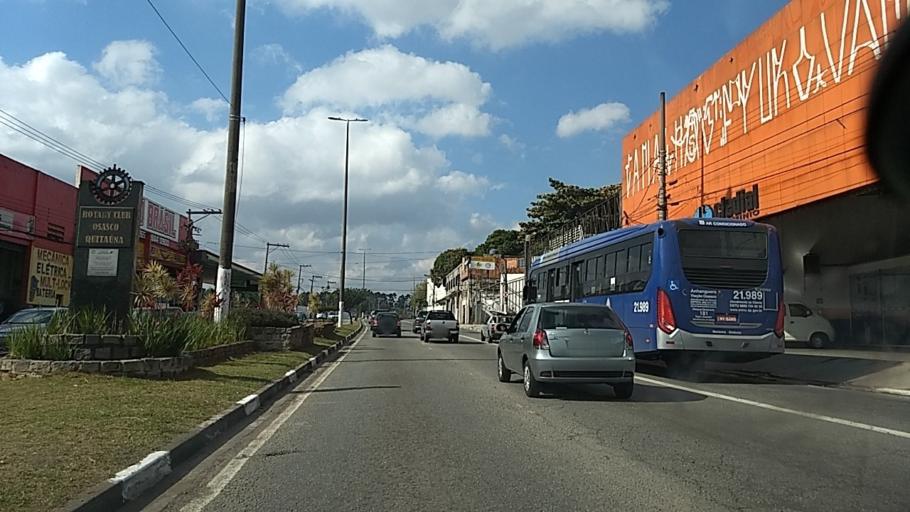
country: BR
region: Sao Paulo
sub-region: Osasco
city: Osasco
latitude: -23.5242
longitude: -46.8111
